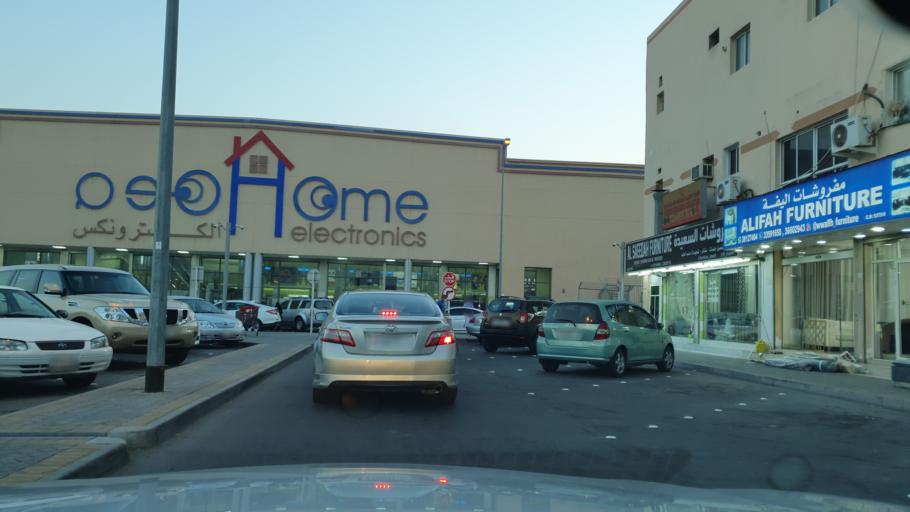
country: BH
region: Northern
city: Madinat `Isa
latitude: 26.1703
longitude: 50.5529
